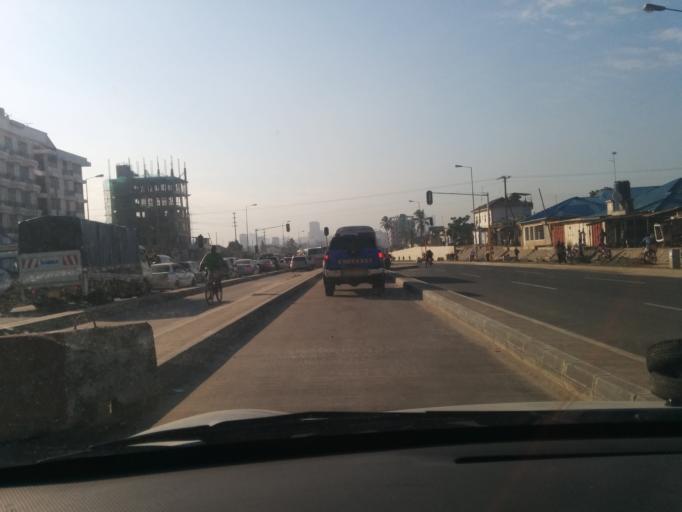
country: TZ
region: Dar es Salaam
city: Magomeni
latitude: -6.8087
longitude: 39.2613
